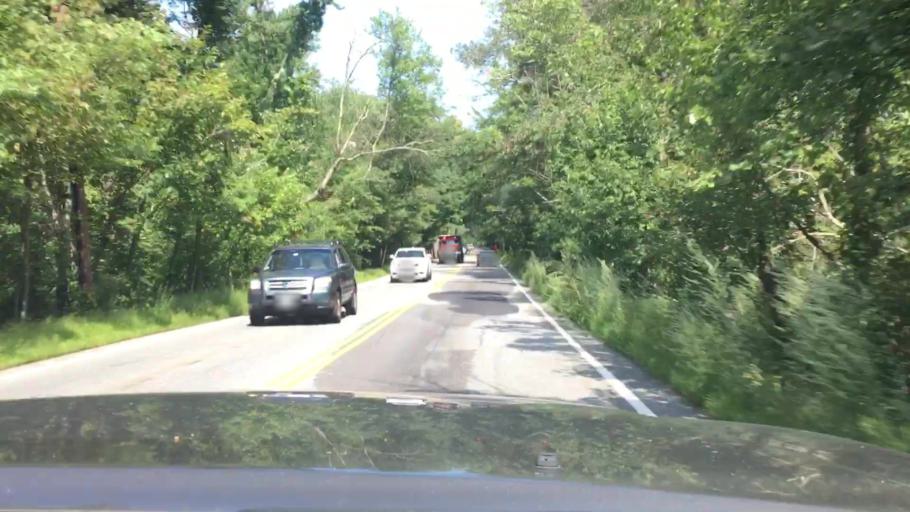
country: US
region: Massachusetts
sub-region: Middlesex County
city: Weston
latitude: 42.3371
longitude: -71.3186
